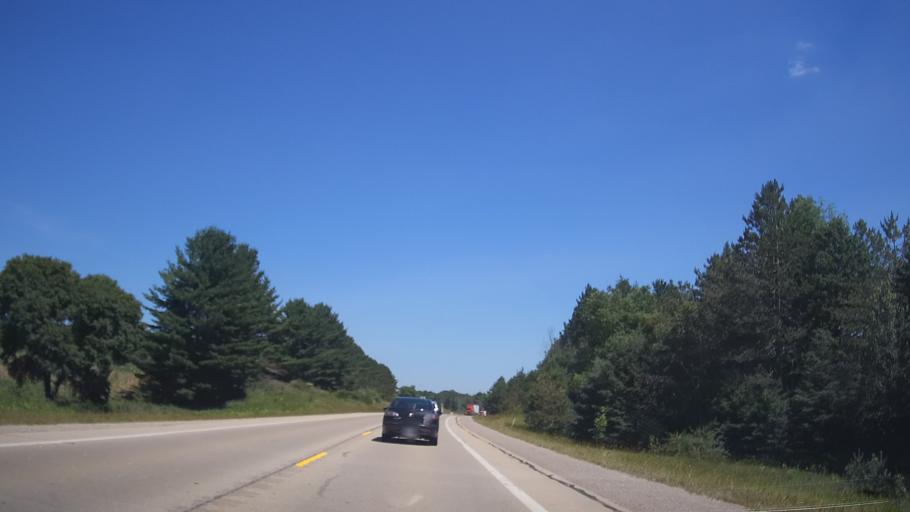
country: US
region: Michigan
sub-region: Clare County
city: Clare
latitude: 43.8697
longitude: -84.9229
